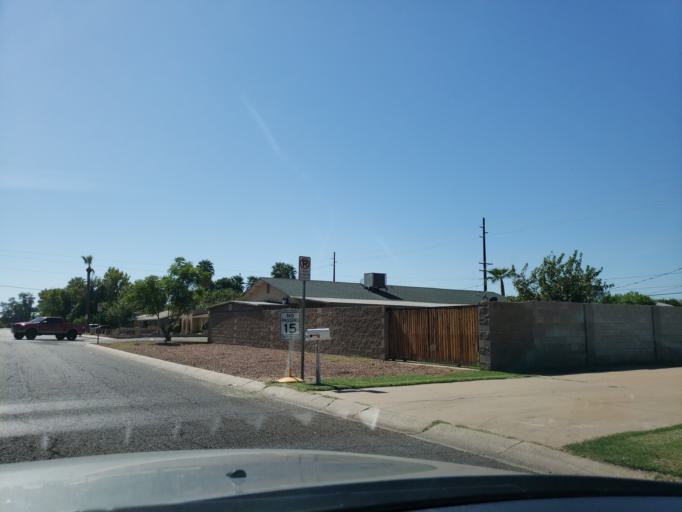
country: US
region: Arizona
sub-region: Maricopa County
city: Glendale
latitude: 33.4846
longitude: -112.1596
